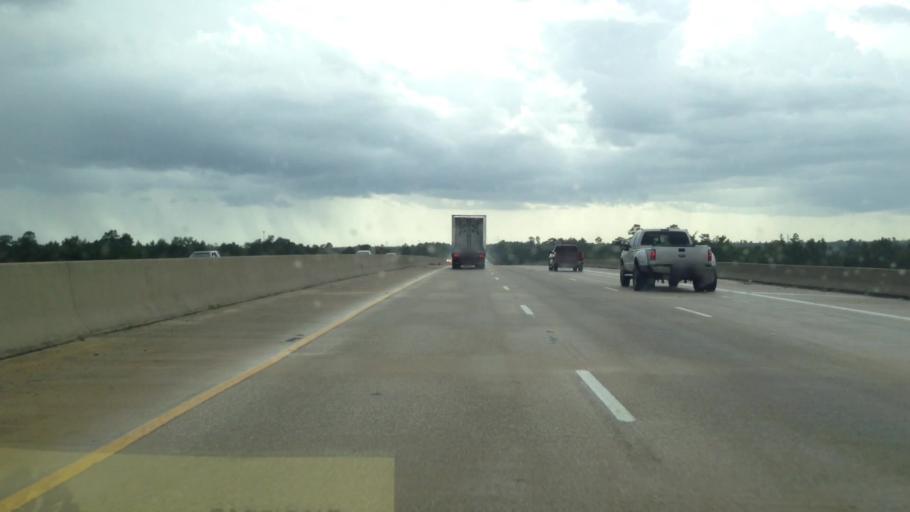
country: US
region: Mississippi
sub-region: Hancock County
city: Diamondhead
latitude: 30.3652
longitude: -89.4014
